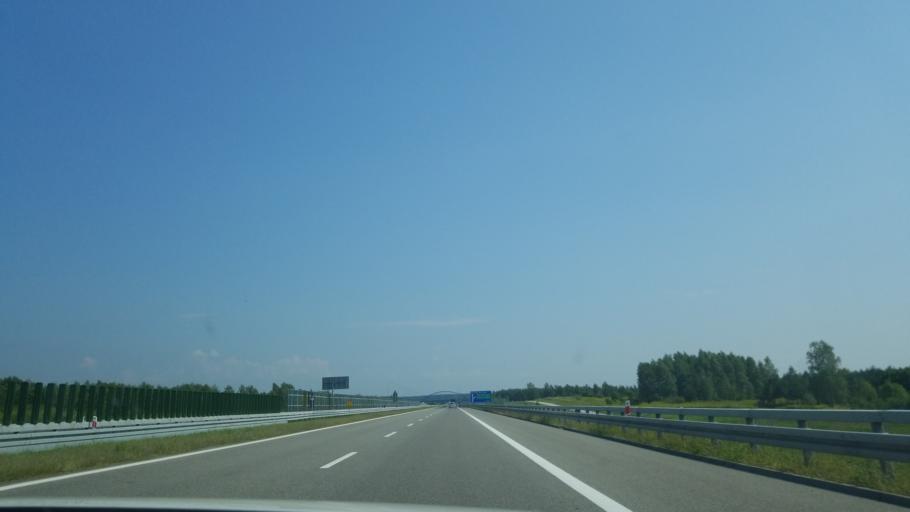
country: PL
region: Subcarpathian Voivodeship
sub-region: Powiat ropczycko-sedziszowski
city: Ostrow
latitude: 50.1093
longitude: 21.6499
